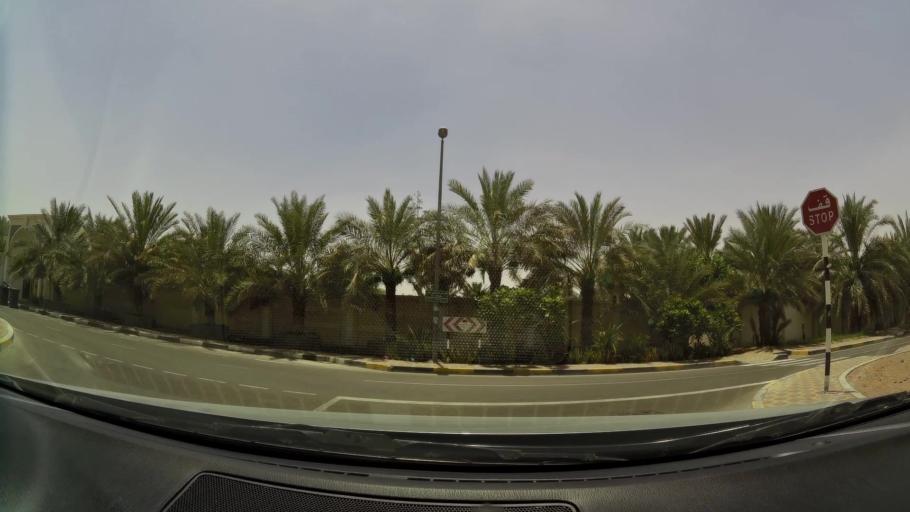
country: OM
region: Al Buraimi
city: Al Buraymi
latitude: 24.2654
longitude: 55.7083
